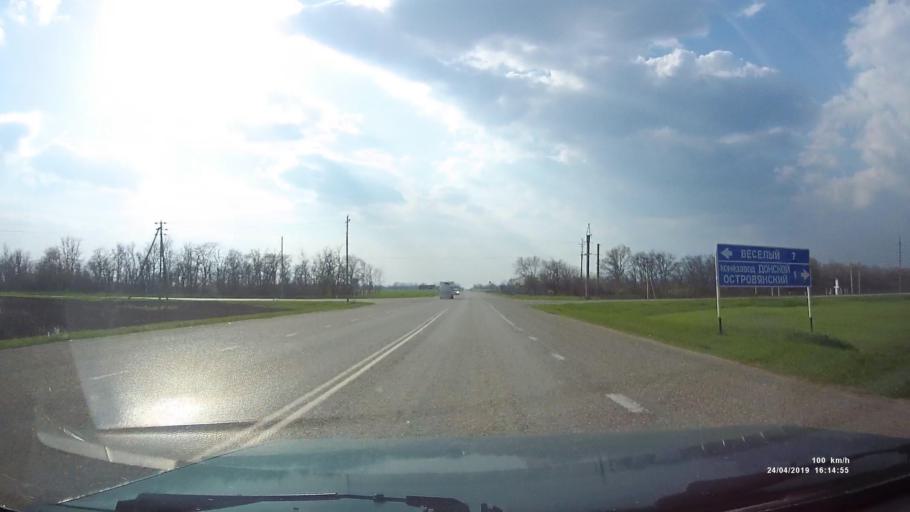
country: RU
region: Rostov
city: Sovetskoye
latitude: 46.7546
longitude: 42.1921
